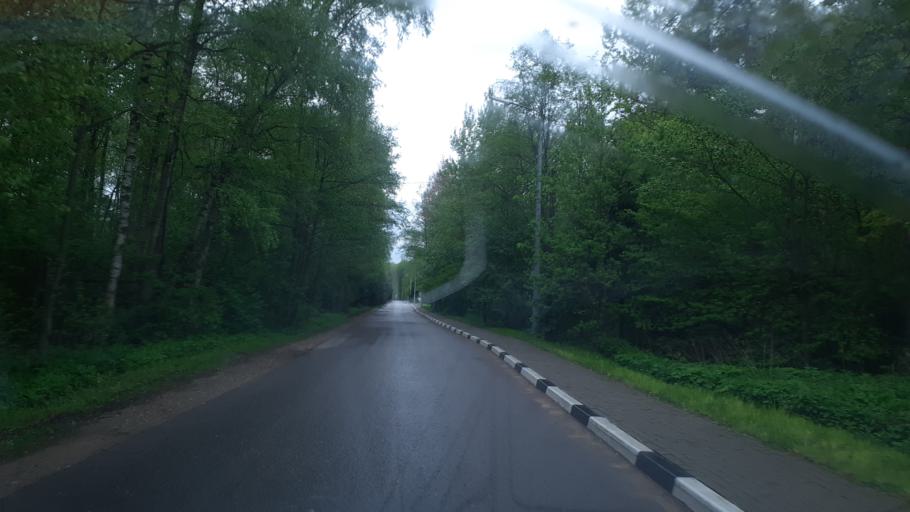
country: RU
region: Moskovskaya
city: Gorki Vtoryye
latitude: 55.7077
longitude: 37.2046
